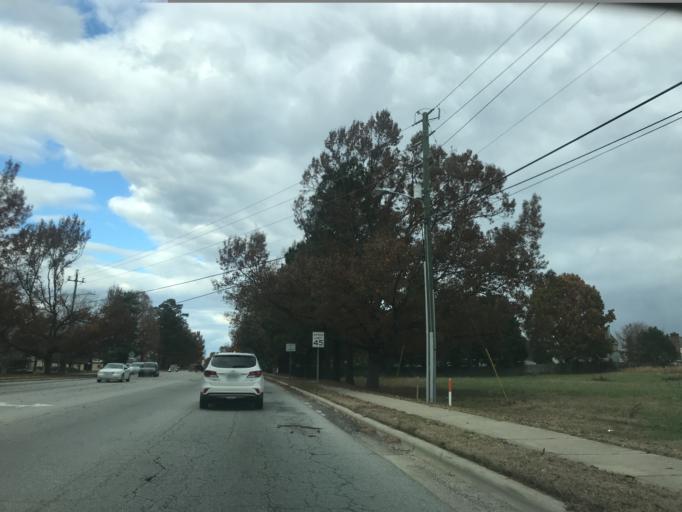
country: US
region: North Carolina
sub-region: Wake County
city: Raleigh
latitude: 35.8317
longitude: -78.5691
